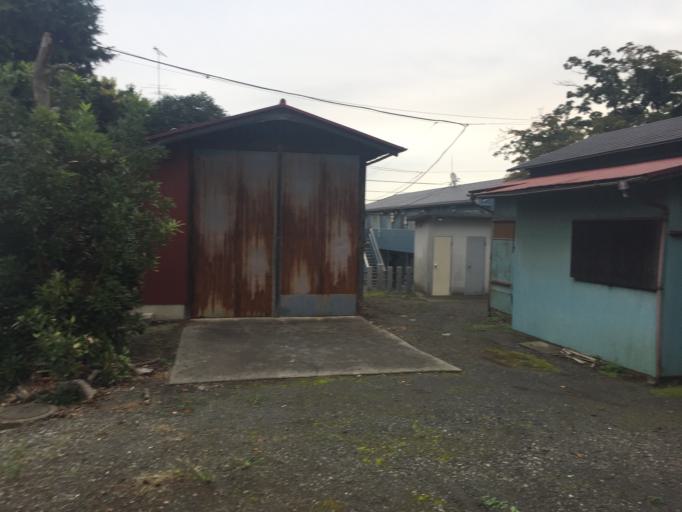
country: JP
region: Tokyo
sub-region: Machida-shi
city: Machida
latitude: 35.5691
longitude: 139.4077
